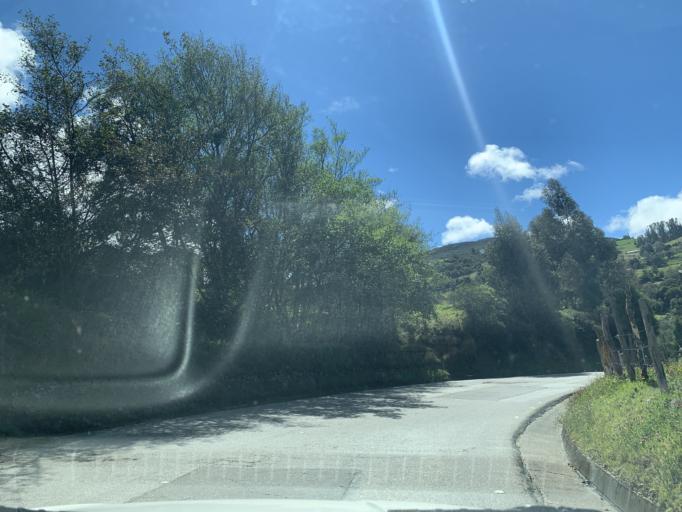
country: CO
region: Boyaca
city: Aquitania
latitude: 5.6159
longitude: -72.8783
